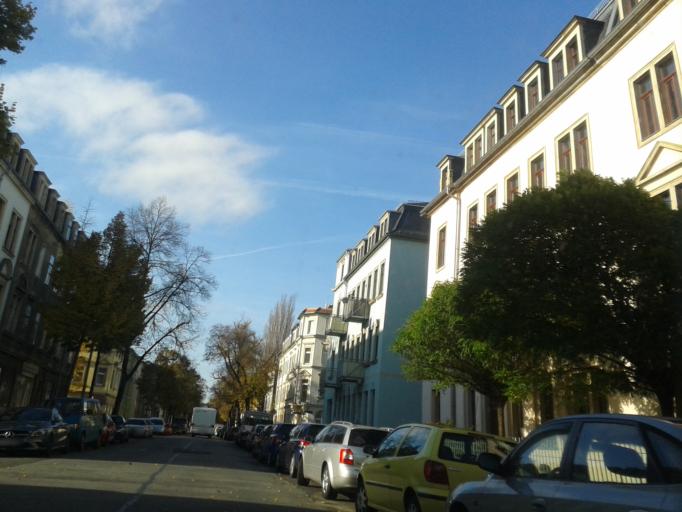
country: DE
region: Saxony
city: Albertstadt
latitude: 51.0891
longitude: 13.7293
